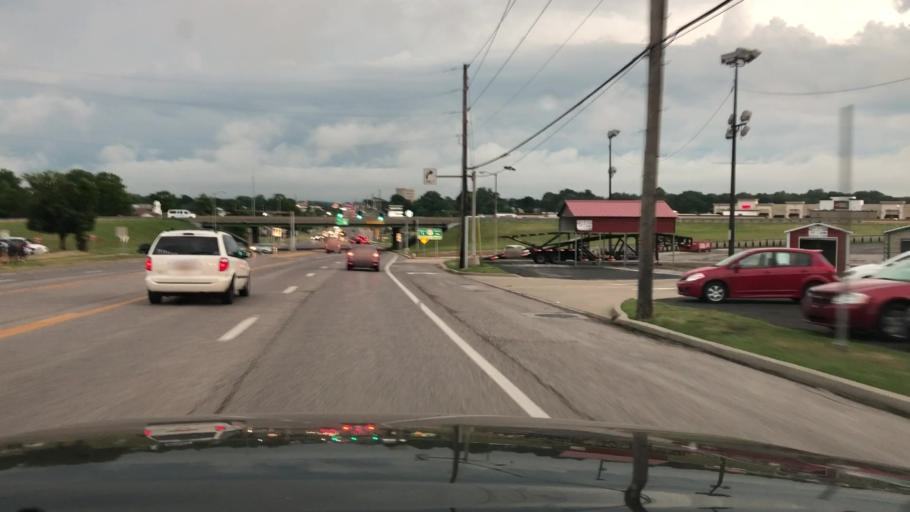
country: US
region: Missouri
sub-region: Saint Louis County
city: Saint Ann
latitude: 38.7387
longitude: -90.4008
